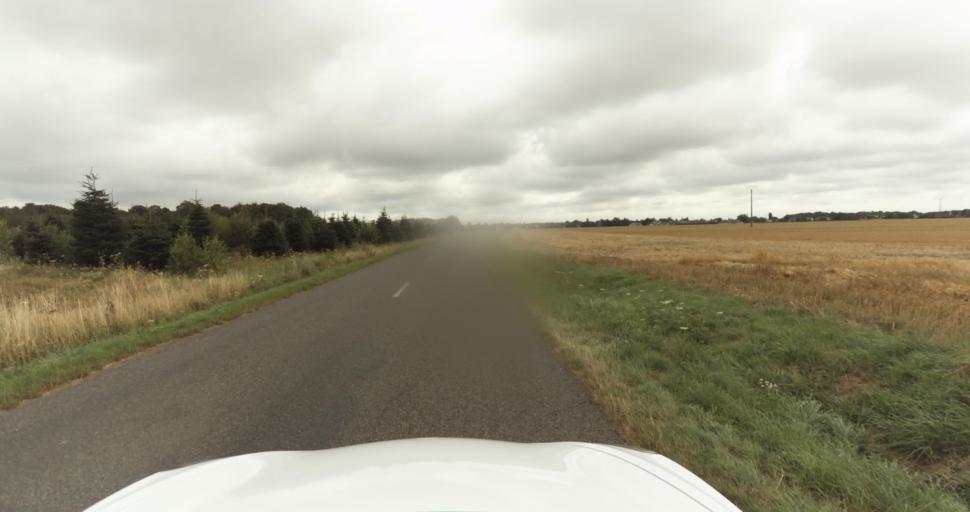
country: FR
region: Haute-Normandie
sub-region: Departement de l'Eure
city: Aviron
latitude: 49.0606
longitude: 1.0786
